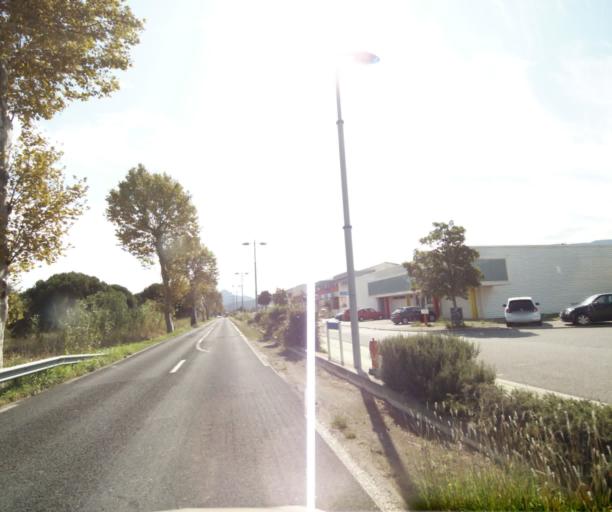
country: FR
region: Languedoc-Roussillon
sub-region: Departement des Pyrenees-Orientales
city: Argelers
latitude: 42.5582
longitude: 3.0109
